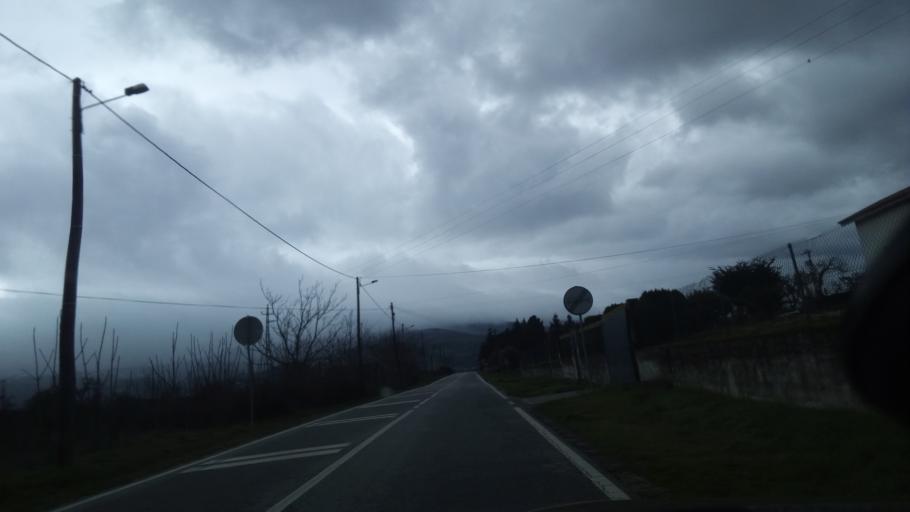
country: PT
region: Guarda
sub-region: Fornos de Algodres
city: Fornos de Algodres
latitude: 40.5554
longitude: -7.5700
